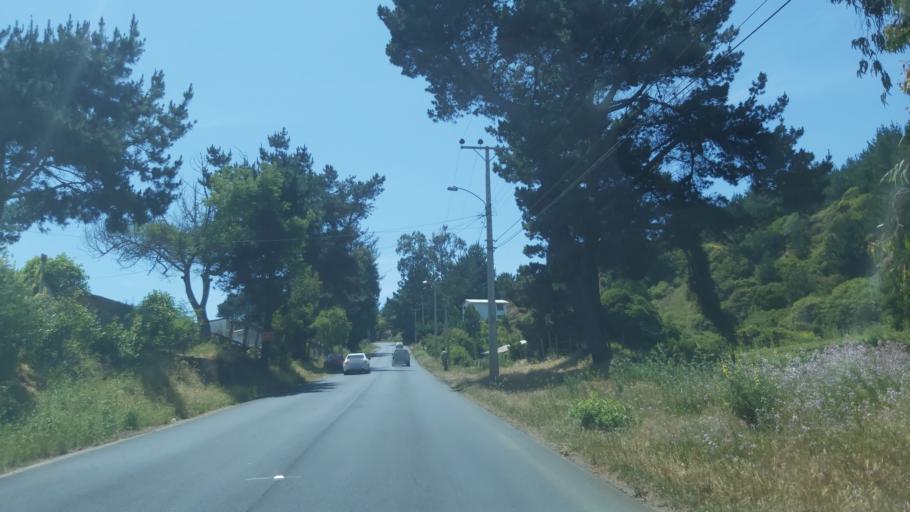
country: CL
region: Maule
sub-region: Provincia de Cauquenes
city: Cauquenes
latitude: -35.8353
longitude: -72.6225
